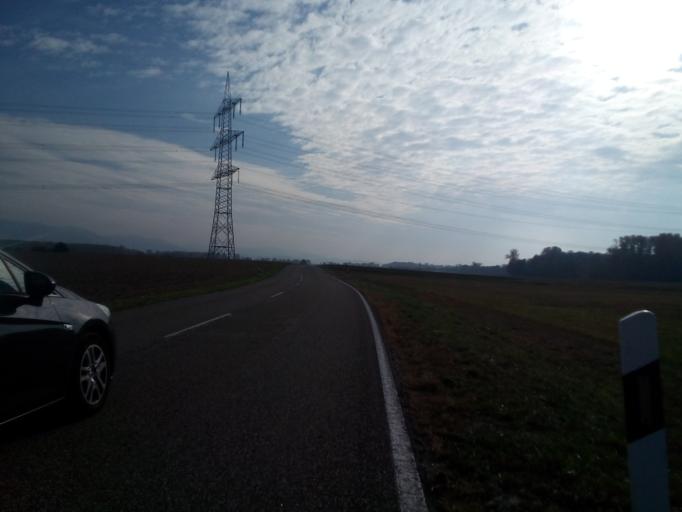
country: DE
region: Baden-Wuerttemberg
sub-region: Karlsruhe Region
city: Zell
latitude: 48.7102
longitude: 8.0686
